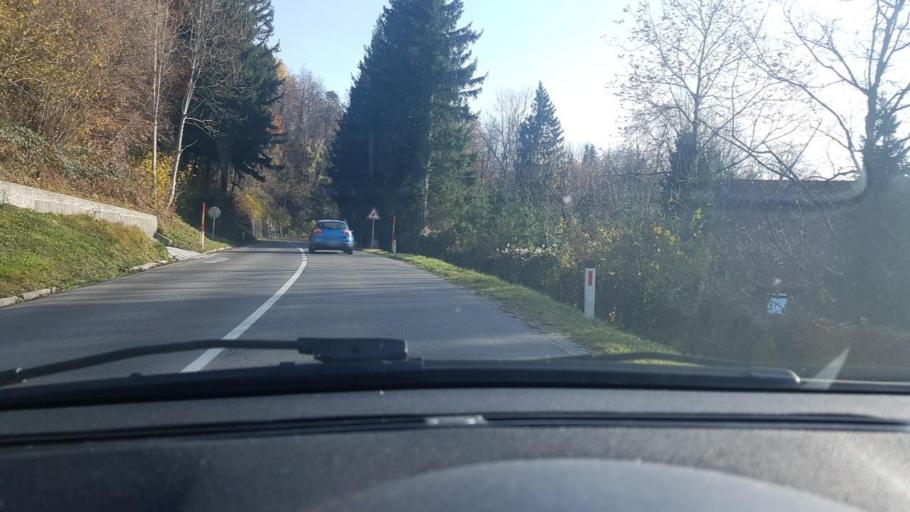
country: SI
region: Trzic
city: Bistrica pri Trzicu
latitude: 46.3355
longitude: 14.3067
